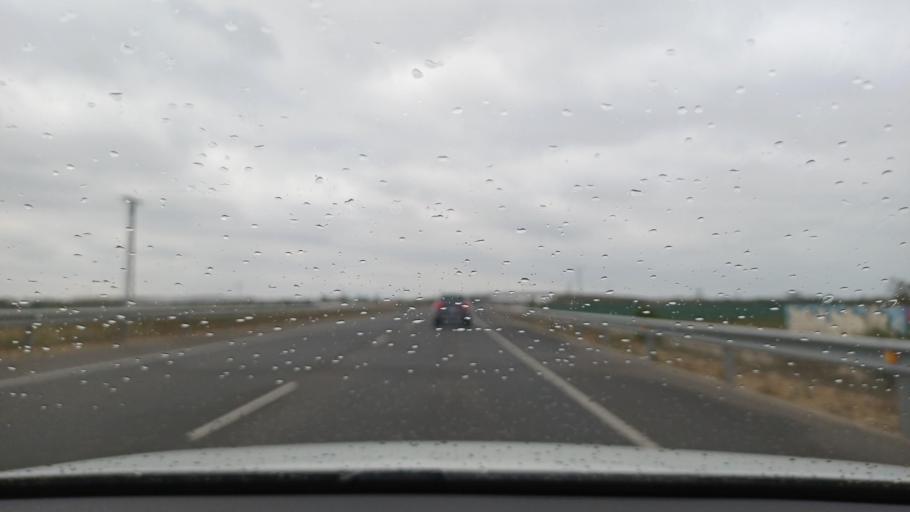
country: ES
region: Valencia
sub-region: Provincia de Castello
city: Benicarlo
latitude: 40.4195
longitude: 0.3878
